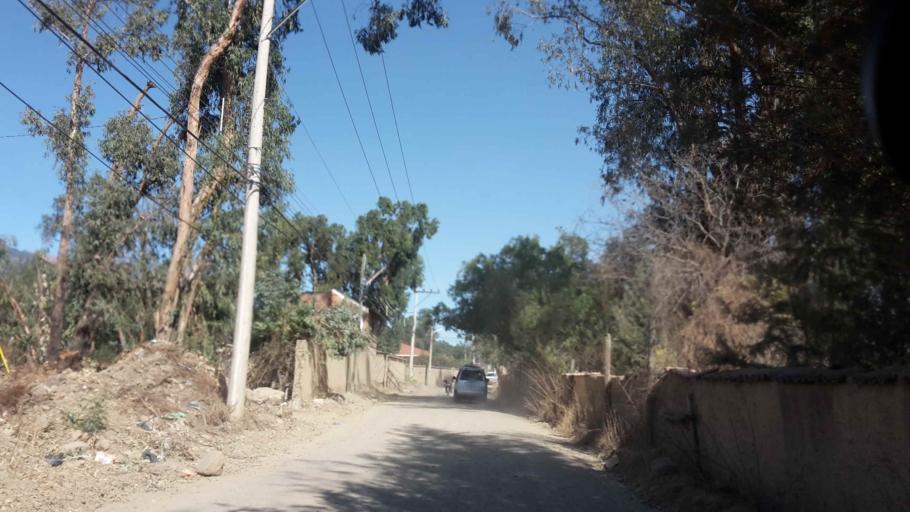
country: BO
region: Cochabamba
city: Cochabamba
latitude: -17.3386
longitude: -66.2088
